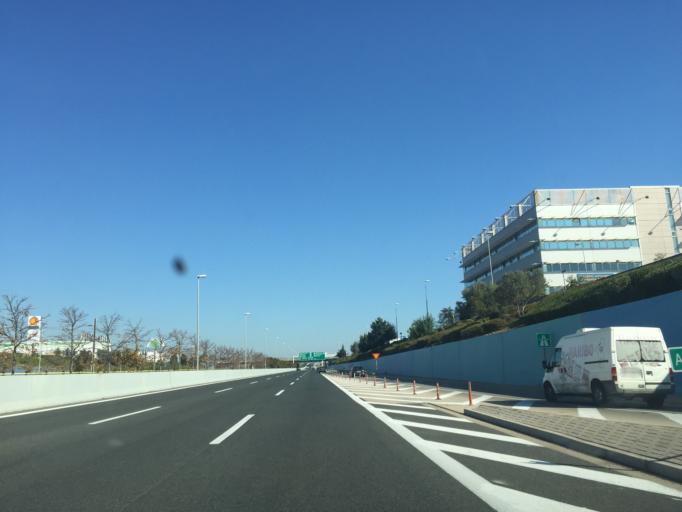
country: GR
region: Attica
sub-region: Nomarchia Anatolikis Attikis
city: Markopoulo
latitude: 37.9240
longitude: 23.9329
